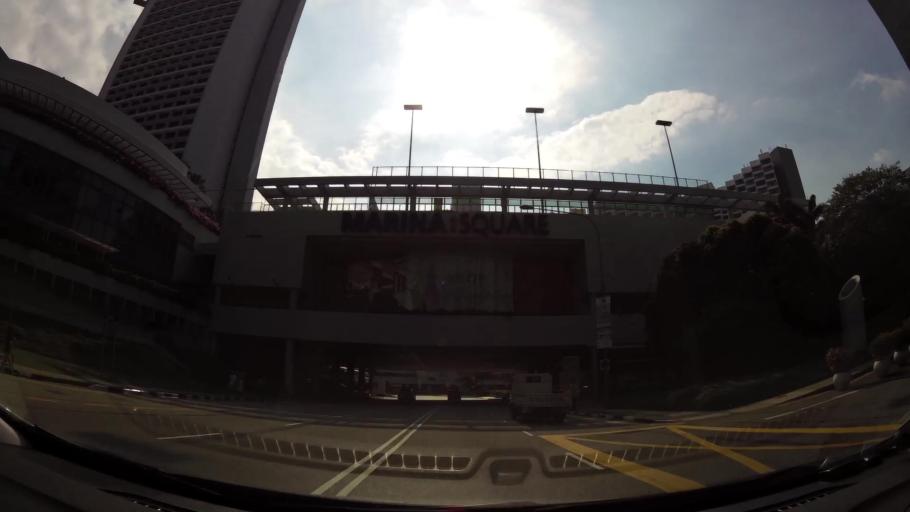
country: SG
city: Singapore
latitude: 1.2921
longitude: 103.8576
